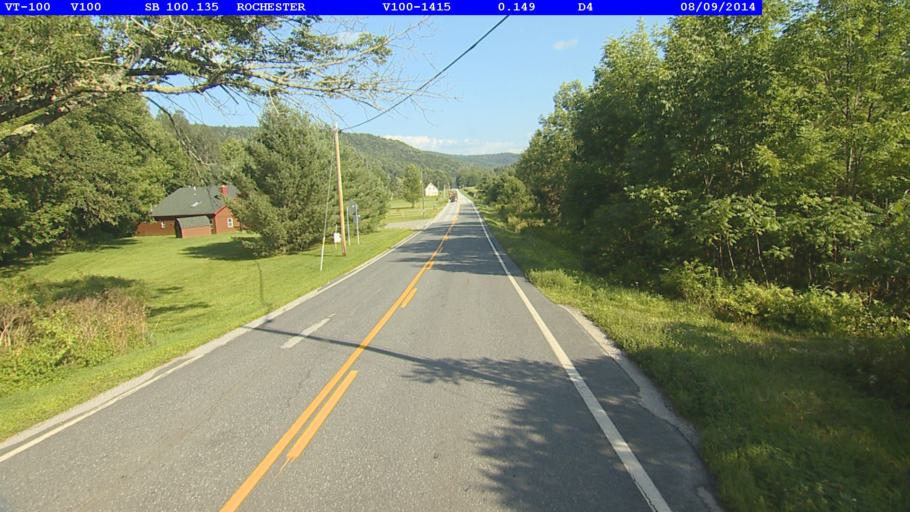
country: US
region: Vermont
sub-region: Orange County
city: Randolph
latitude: 43.8068
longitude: -72.7843
